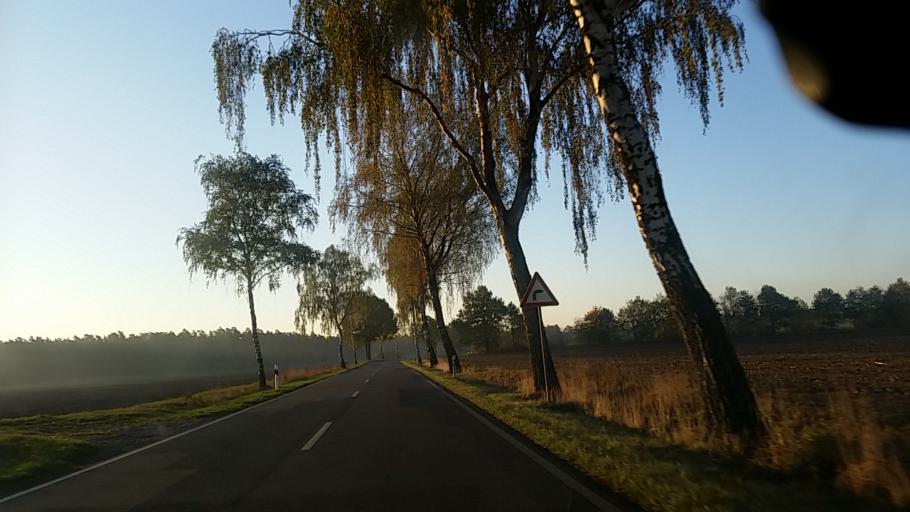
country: DE
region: Lower Saxony
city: Tulau
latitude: 52.6499
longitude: 10.8070
